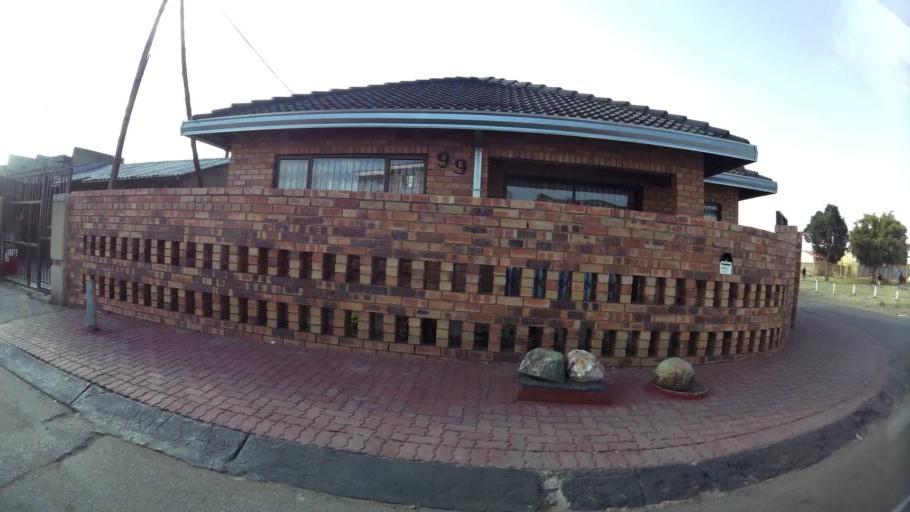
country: ZA
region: Gauteng
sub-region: City of Johannesburg Metropolitan Municipality
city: Soweto
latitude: -26.2585
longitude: 27.9065
